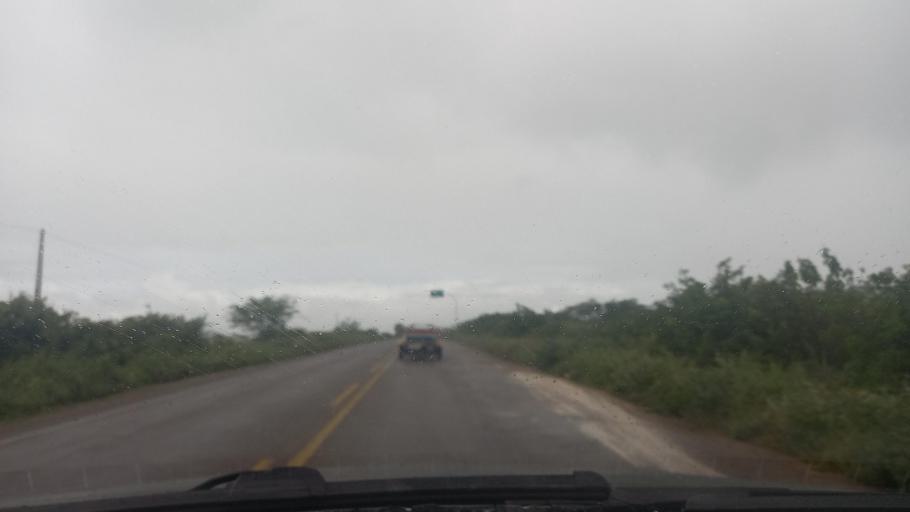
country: BR
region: Bahia
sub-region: Paulo Afonso
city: Paulo Afonso
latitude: -9.3545
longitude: -38.2775
